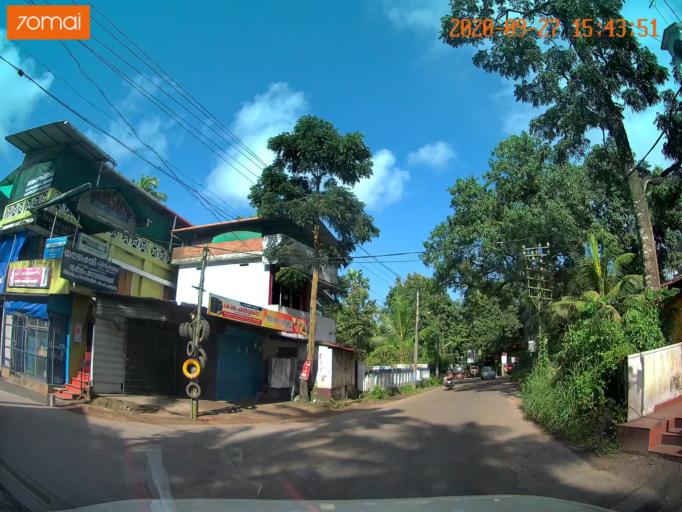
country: IN
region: Kerala
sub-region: Thrissur District
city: Thanniyam
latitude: 10.4752
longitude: 76.1107
